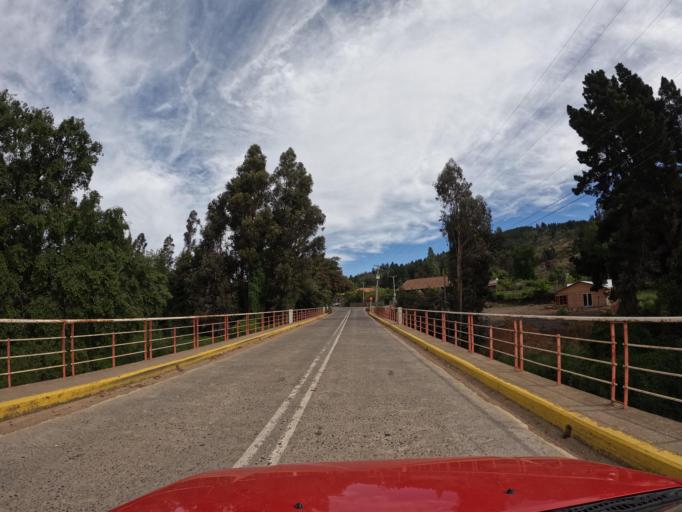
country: CL
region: Maule
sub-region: Provincia de Talca
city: Talca
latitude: -35.3194
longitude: -71.9582
